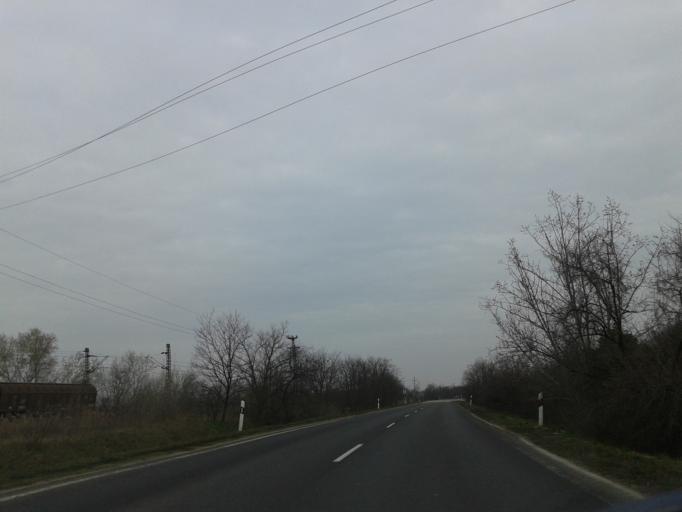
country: HU
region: Komarom-Esztergom
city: Szomod
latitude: 47.6768
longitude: 18.3202
